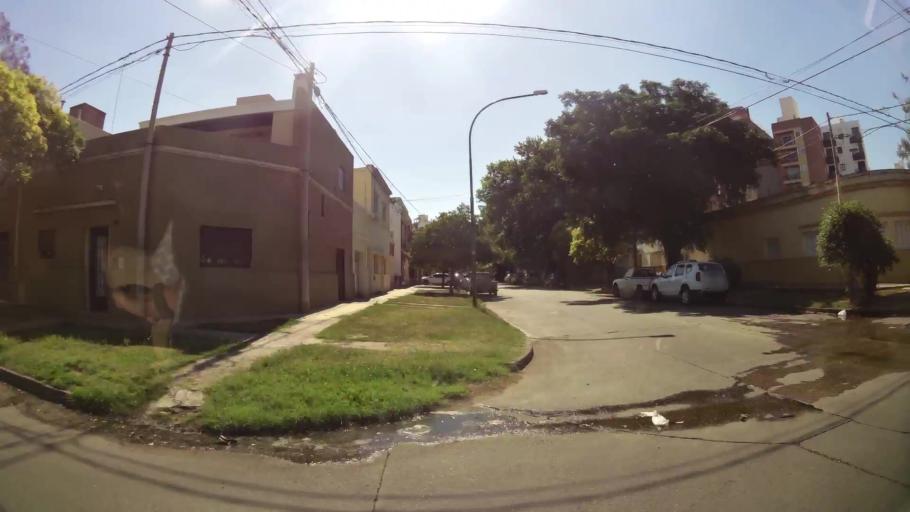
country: AR
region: Cordoba
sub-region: Departamento de Capital
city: Cordoba
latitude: -31.4173
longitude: -64.1667
